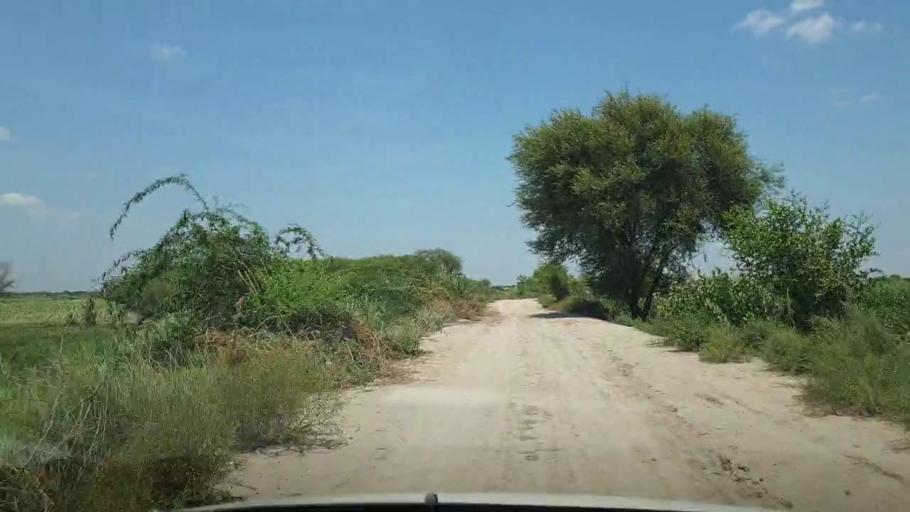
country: PK
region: Sindh
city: Sanghar
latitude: 26.1028
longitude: 69.0028
